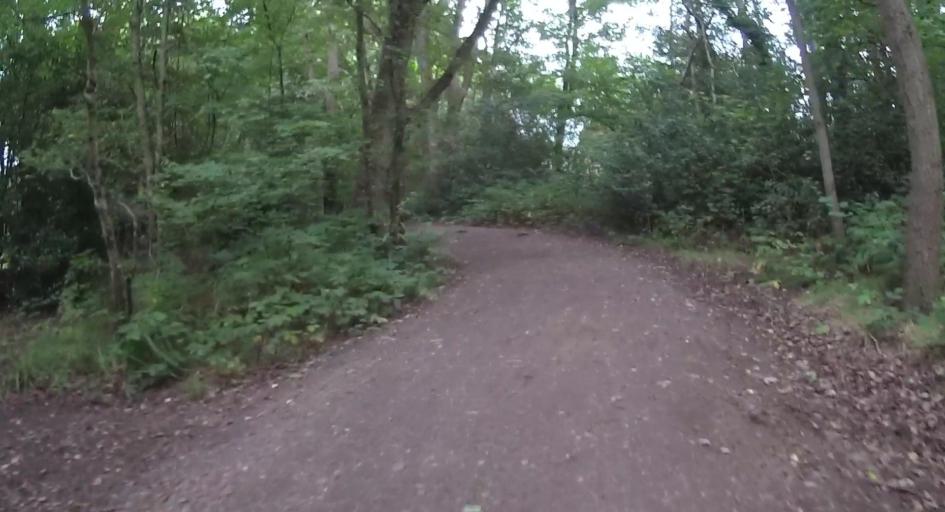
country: GB
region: England
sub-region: Surrey
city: Woking
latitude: 51.3403
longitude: -0.5620
